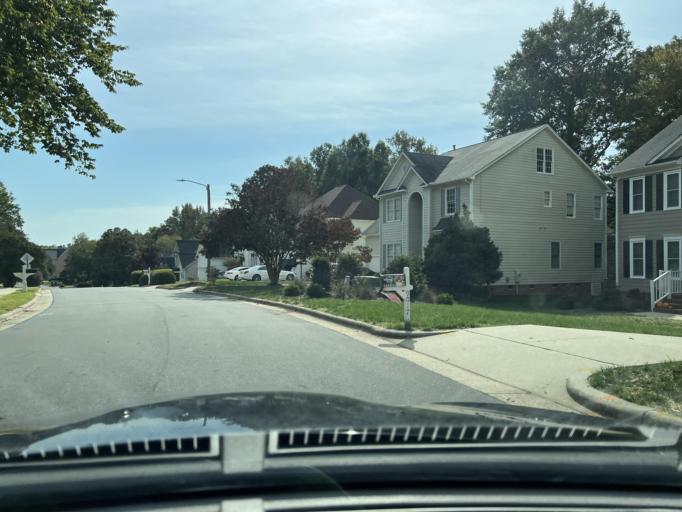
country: US
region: North Carolina
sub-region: Wake County
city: Wake Forest
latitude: 35.9009
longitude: -78.5830
